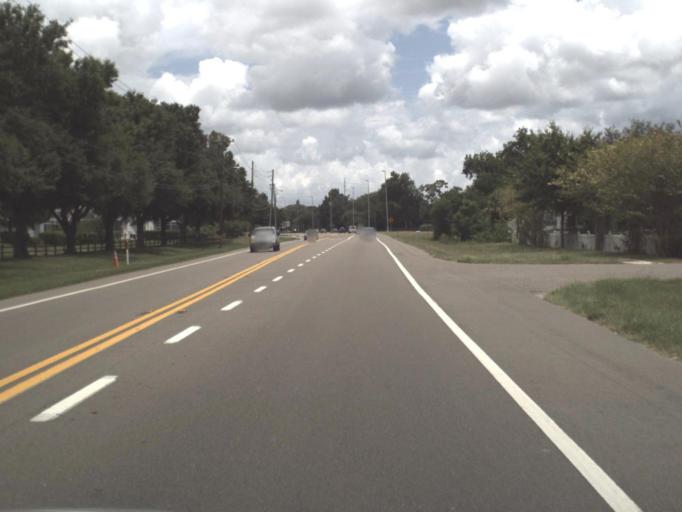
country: US
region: Florida
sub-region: Pinellas County
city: Palm Harbor
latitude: 28.0494
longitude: -82.7666
